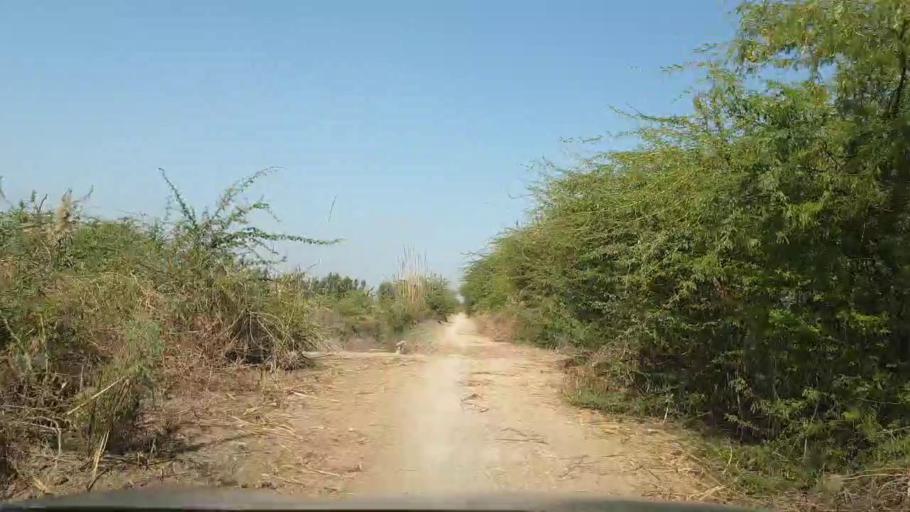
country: PK
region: Sindh
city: Berani
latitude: 25.6830
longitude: 68.8953
